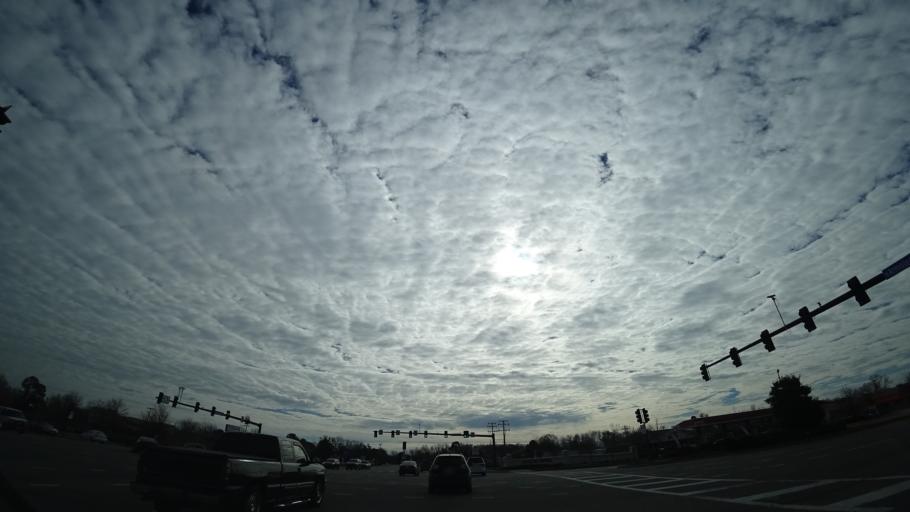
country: US
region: Virginia
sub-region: City of Hampton
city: Hampton
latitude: 37.0442
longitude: -76.3772
